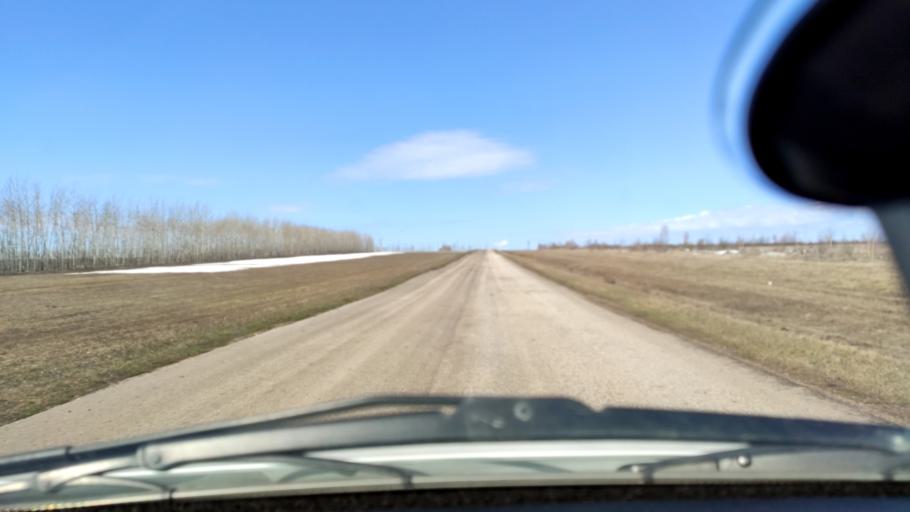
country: RU
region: Bashkortostan
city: Tolbazy
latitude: 54.1710
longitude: 55.9104
